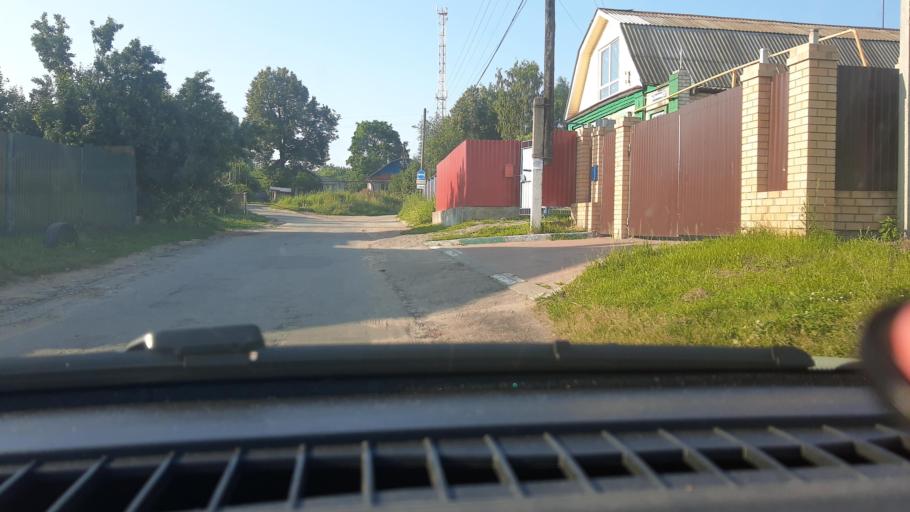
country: RU
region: Nizjnij Novgorod
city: Nizhniy Novgorod
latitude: 56.1896
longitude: 43.9434
